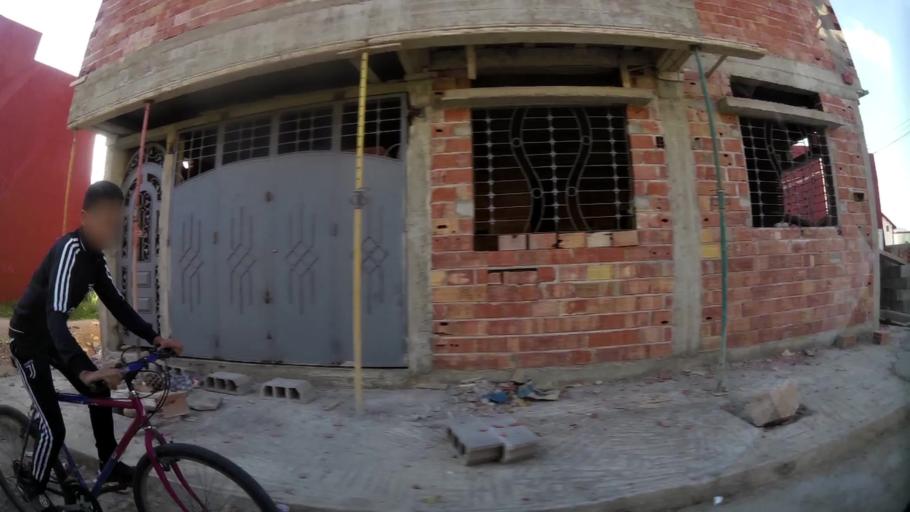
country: MA
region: Oriental
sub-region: Oujda-Angad
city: Oujda
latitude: 34.6966
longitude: -1.9138
